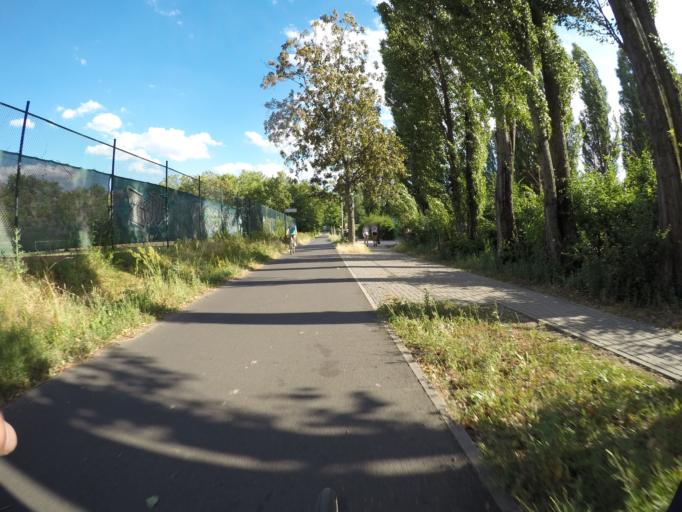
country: DE
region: Berlin
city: Markisches Viertel
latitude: 52.6001
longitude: 13.3502
